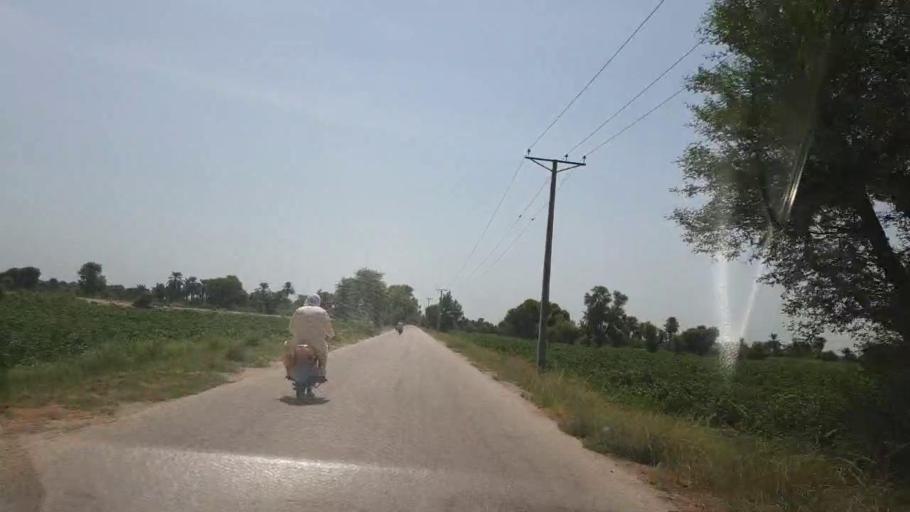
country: PK
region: Sindh
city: Bozdar
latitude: 27.0612
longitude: 68.5751
